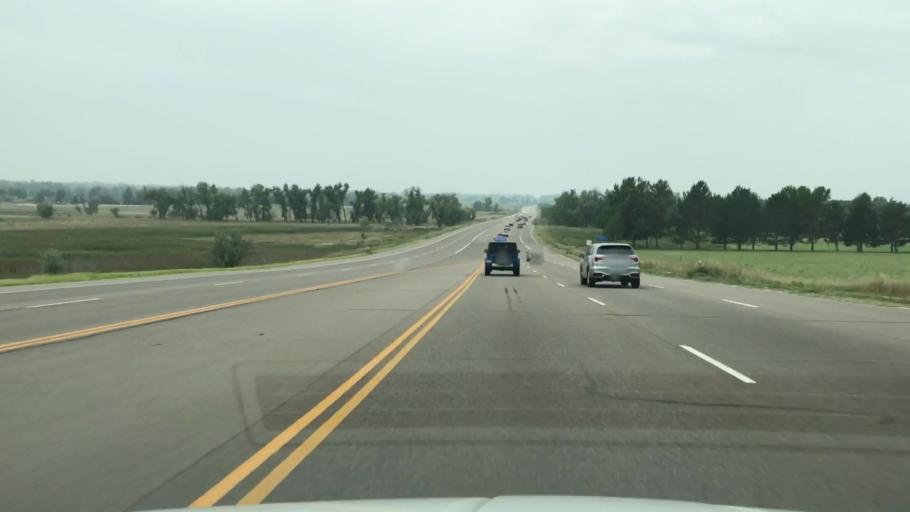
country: US
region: Colorado
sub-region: Boulder County
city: Erie
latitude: 40.0637
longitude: -105.1028
